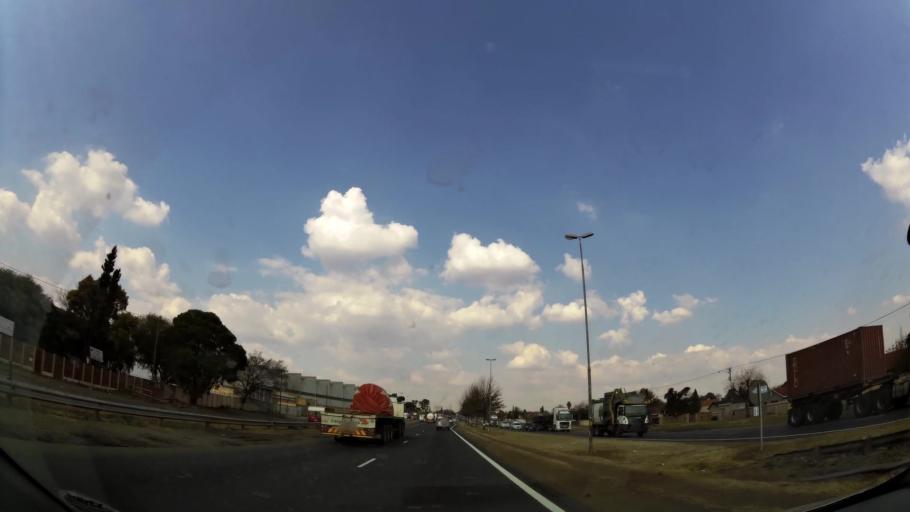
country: ZA
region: Gauteng
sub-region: Ekurhuleni Metropolitan Municipality
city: Germiston
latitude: -26.2960
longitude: 28.1759
